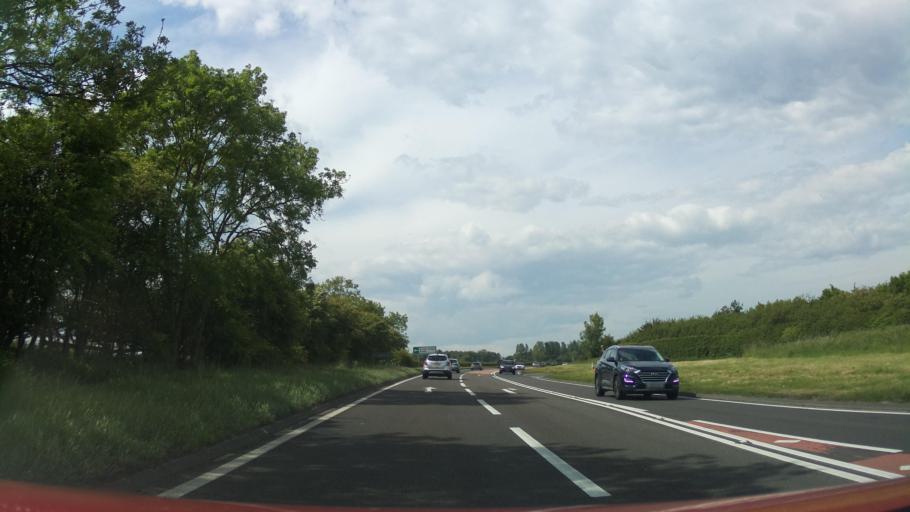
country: GB
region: England
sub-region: Northumberland
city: Felton
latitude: 55.2726
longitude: -1.7238
